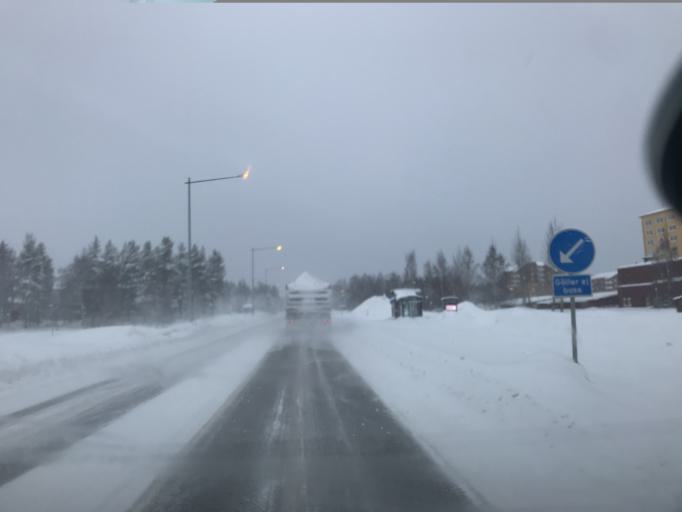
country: SE
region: Norrbotten
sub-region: Lulea Kommun
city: Lulea
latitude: 65.6162
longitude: 22.1317
